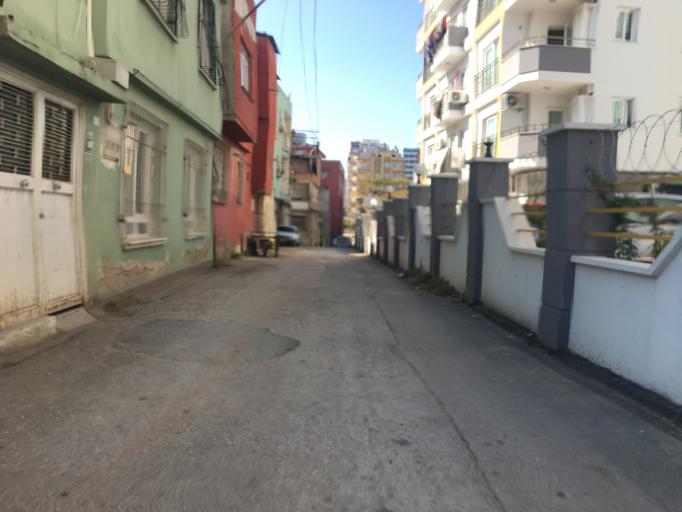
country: TR
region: Adana
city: Seyhan
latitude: 37.0295
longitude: 35.2886
